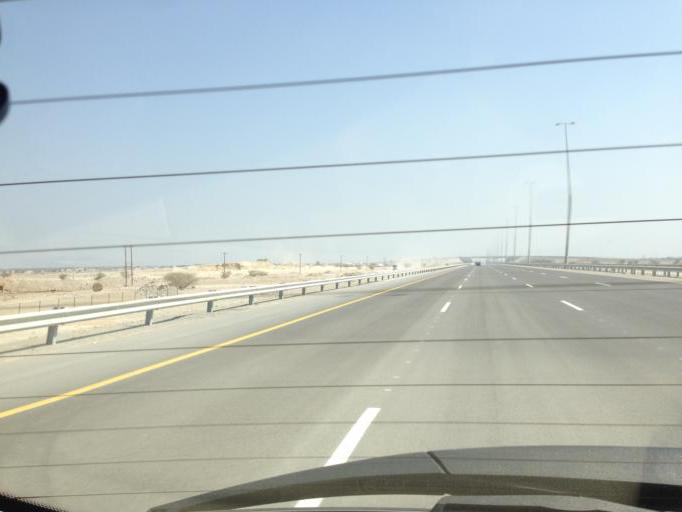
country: OM
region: Al Batinah
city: Barka'
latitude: 23.6167
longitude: 57.8361
